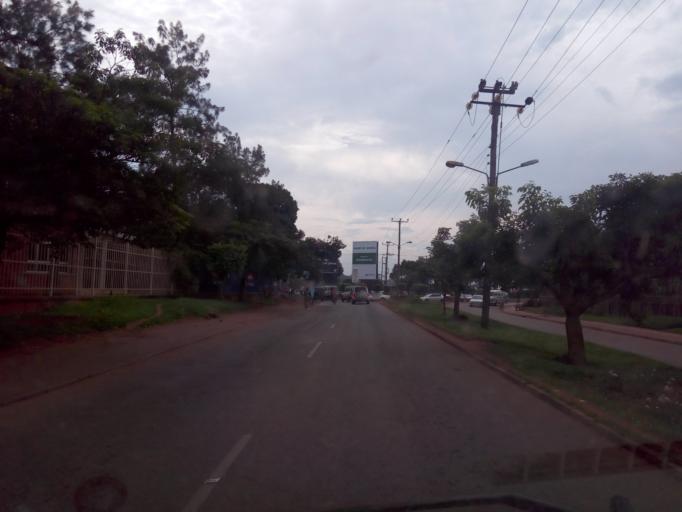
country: UG
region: Central Region
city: Kampala Central Division
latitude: 0.3332
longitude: 32.5777
